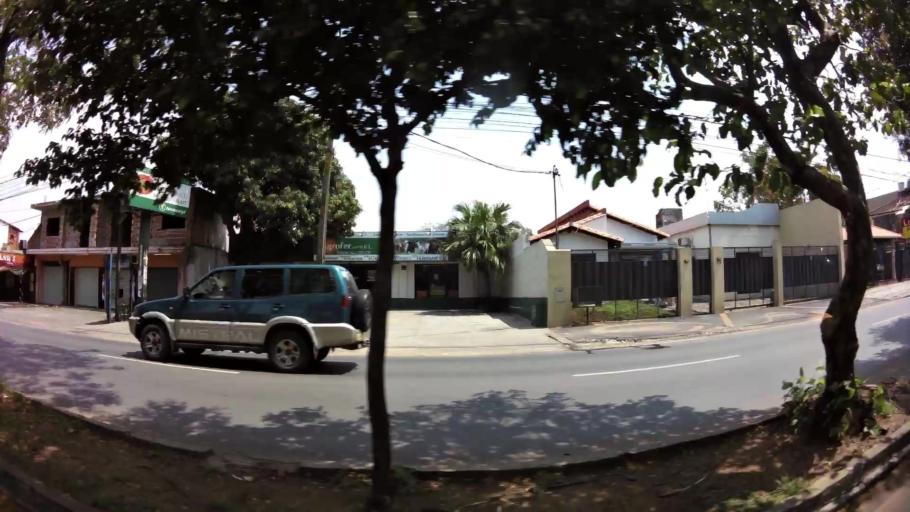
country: PY
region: Central
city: Lambare
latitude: -25.3183
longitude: -57.5917
